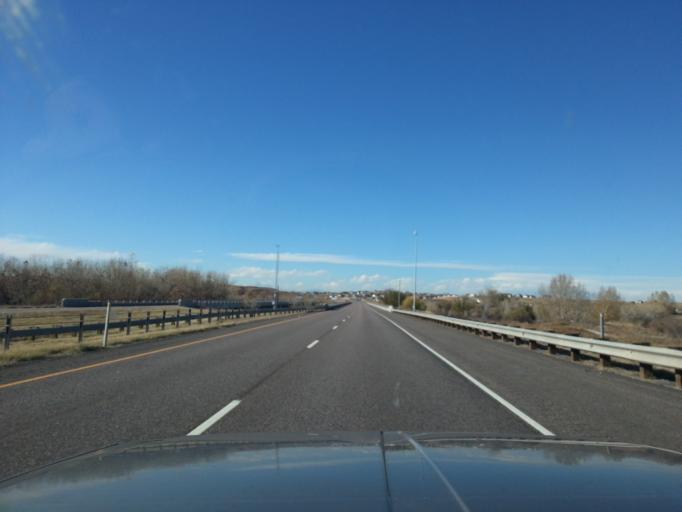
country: US
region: Colorado
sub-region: Adams County
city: Todd Creek
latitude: 39.9458
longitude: -104.8564
